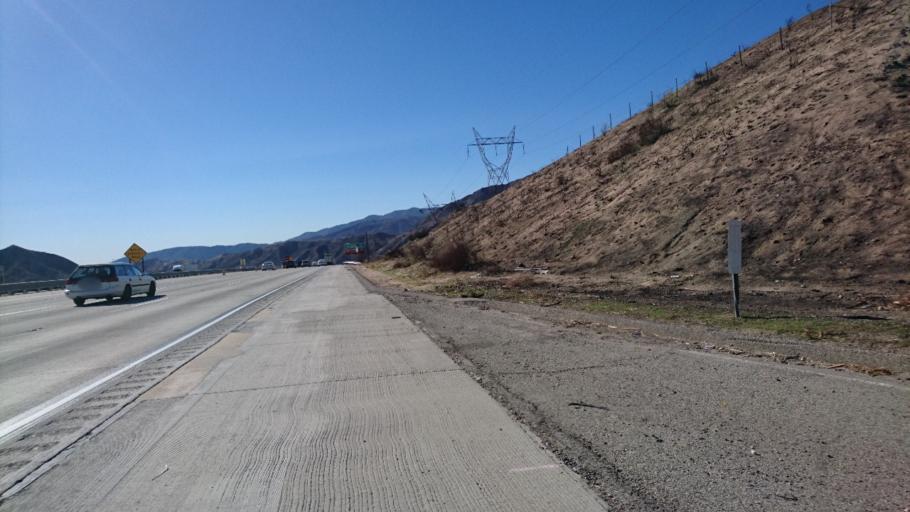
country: US
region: California
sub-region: San Bernardino County
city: Oak Hills
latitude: 34.3315
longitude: -117.4826
